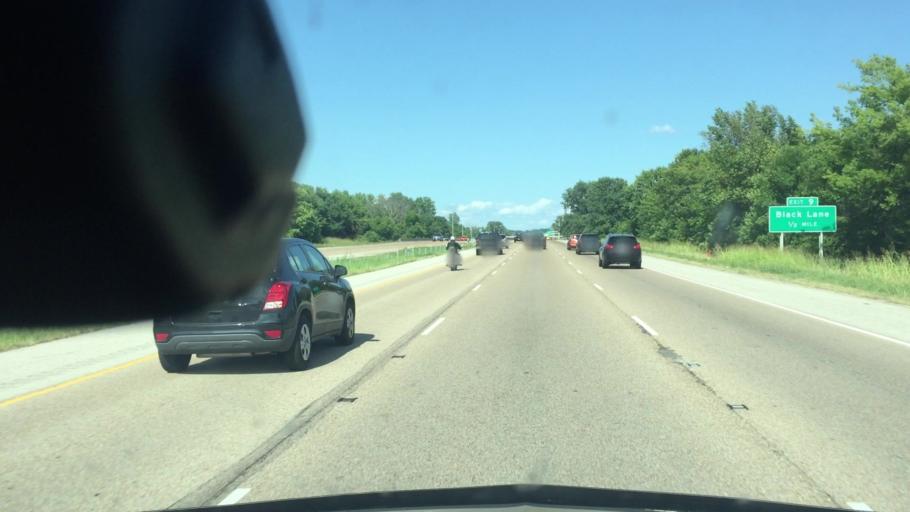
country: US
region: Illinois
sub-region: Saint Clair County
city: Fairmont City
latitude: 38.6649
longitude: -90.0580
